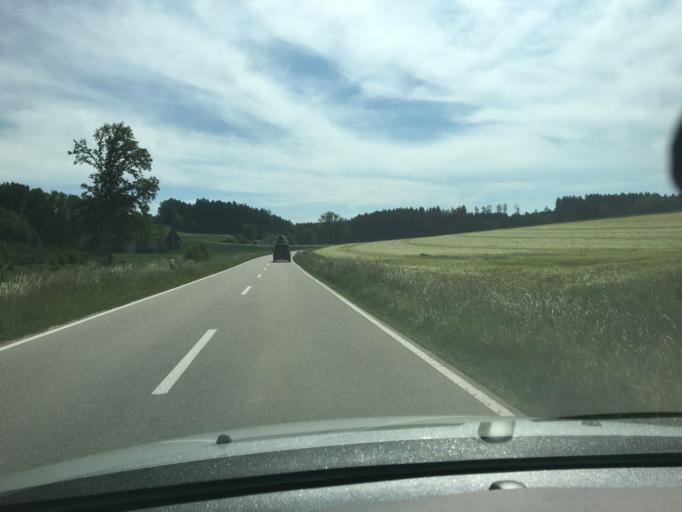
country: DE
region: Bavaria
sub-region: Lower Bavaria
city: Massing
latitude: 48.3620
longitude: 12.5859
